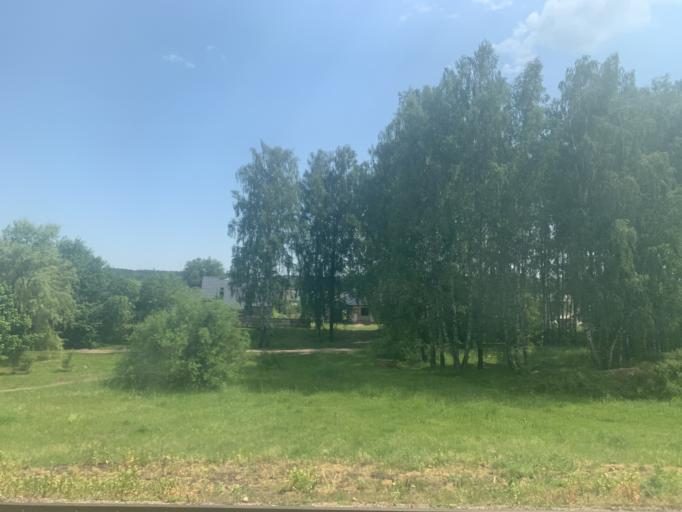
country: BY
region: Minsk
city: Stowbtsy
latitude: 53.4909
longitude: 26.7687
